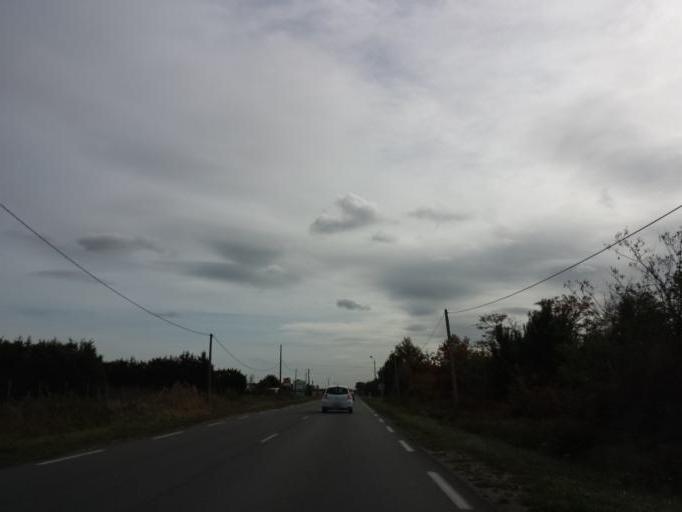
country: FR
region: Aquitaine
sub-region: Departement de la Gironde
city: Marcheprime
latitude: 44.7724
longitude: -0.9274
